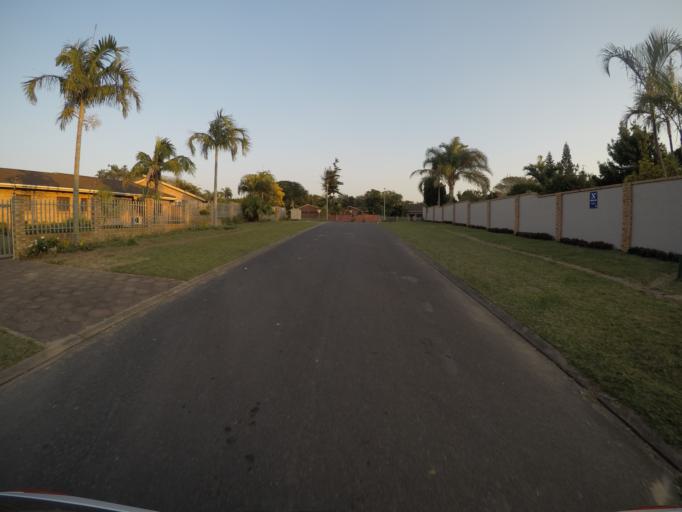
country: ZA
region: KwaZulu-Natal
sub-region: uThungulu District Municipality
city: Richards Bay
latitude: -28.7650
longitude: 32.1170
